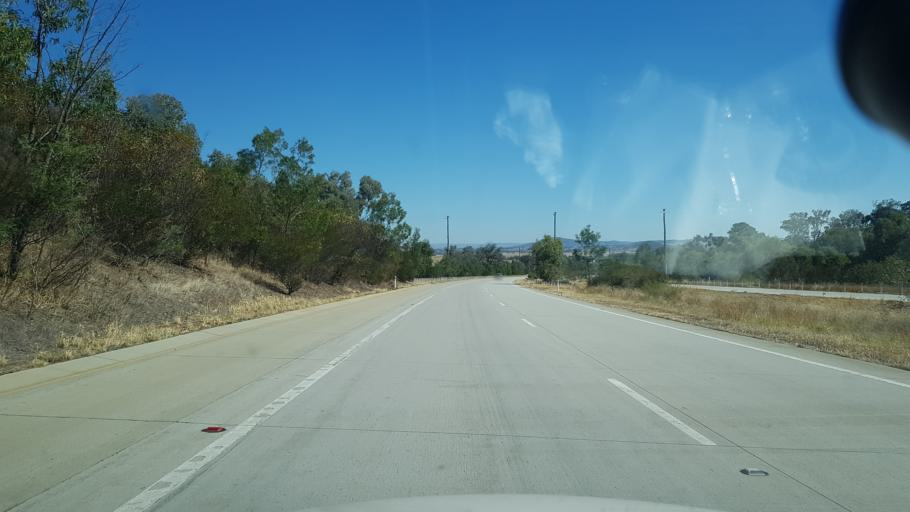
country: AU
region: New South Wales
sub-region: Albury Municipality
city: Lavington
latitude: -35.9221
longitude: 147.0936
